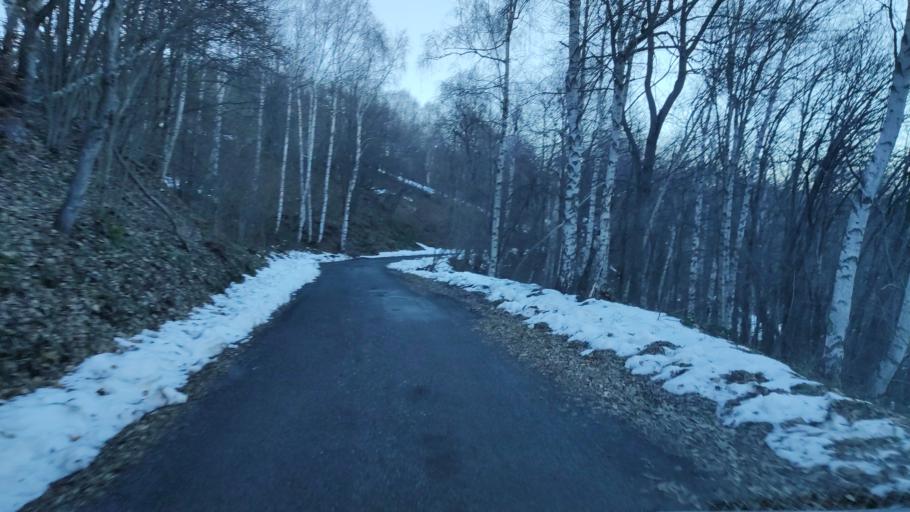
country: IT
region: Piedmont
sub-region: Provincia di Cuneo
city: Viola
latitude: 44.2719
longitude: 7.9921
